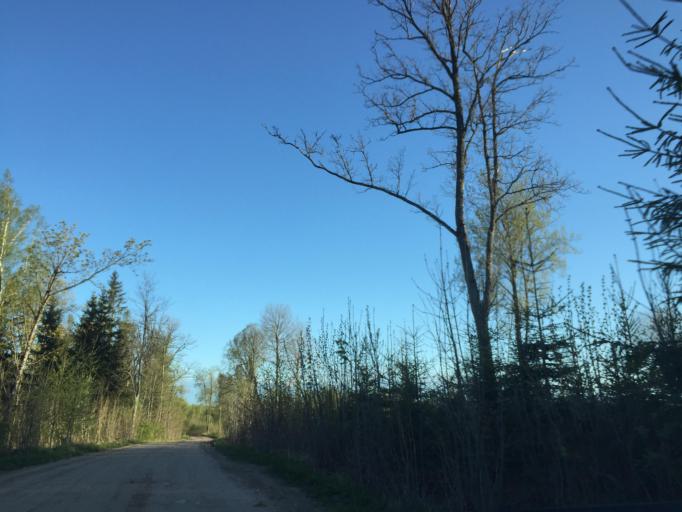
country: LV
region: Vecpiebalga
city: Vecpiebalga
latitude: 56.8481
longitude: 25.9577
